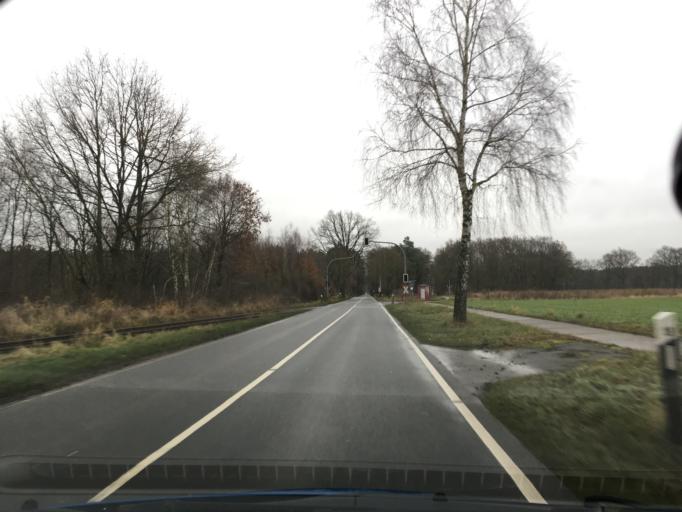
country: DE
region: Lower Saxony
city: Neetze
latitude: 53.2795
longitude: 10.6385
